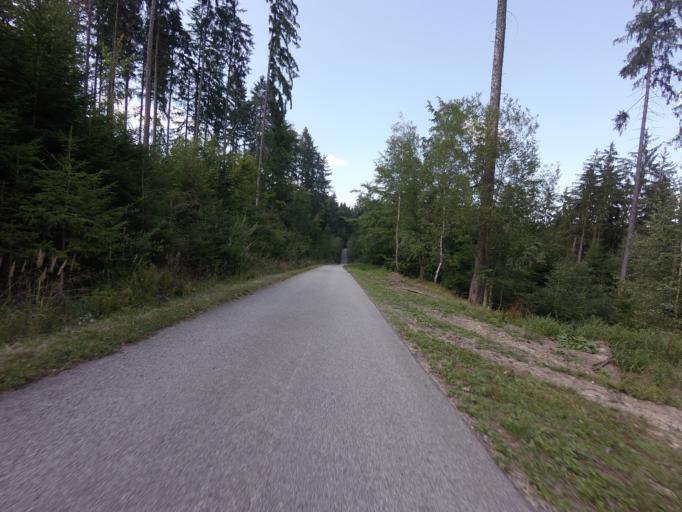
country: CZ
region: Jihocesky
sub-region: Okres Ceske Budejovice
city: Hluboka nad Vltavou
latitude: 49.1060
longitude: 14.4605
